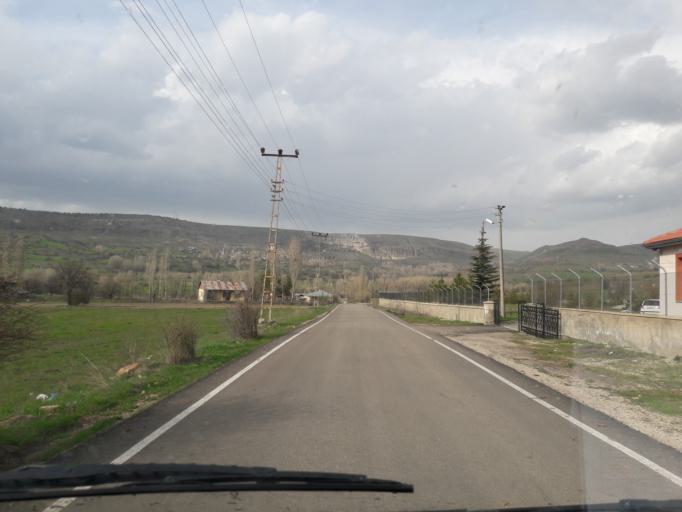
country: TR
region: Giresun
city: Alucra
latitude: 40.3267
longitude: 38.7726
